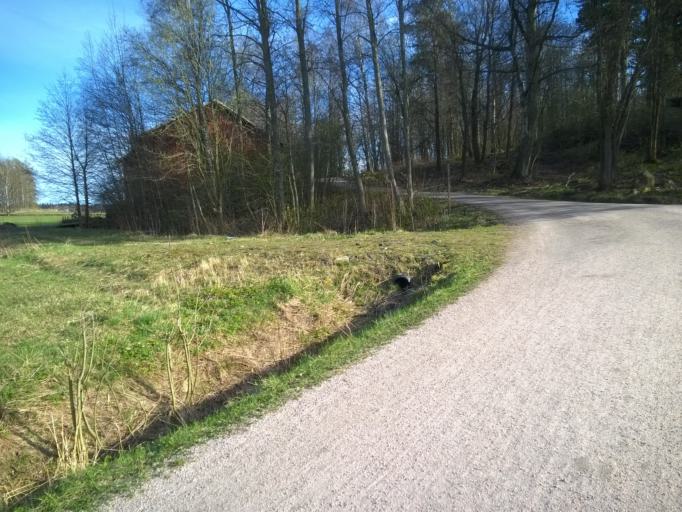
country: FI
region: Uusimaa
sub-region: Helsinki
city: Vantaa
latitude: 60.2216
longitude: 25.0084
